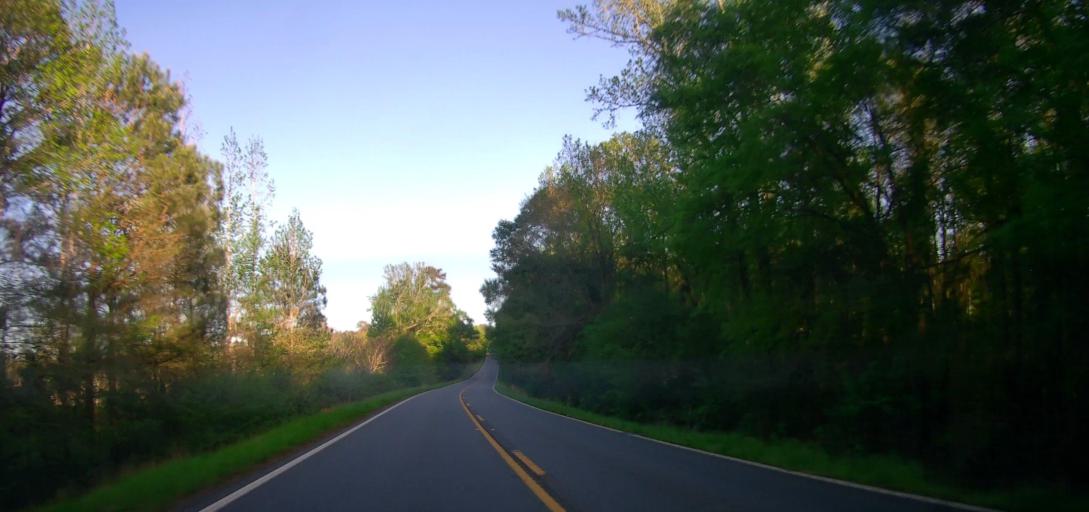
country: US
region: Georgia
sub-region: Marion County
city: Buena Vista
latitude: 32.3676
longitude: -84.4155
